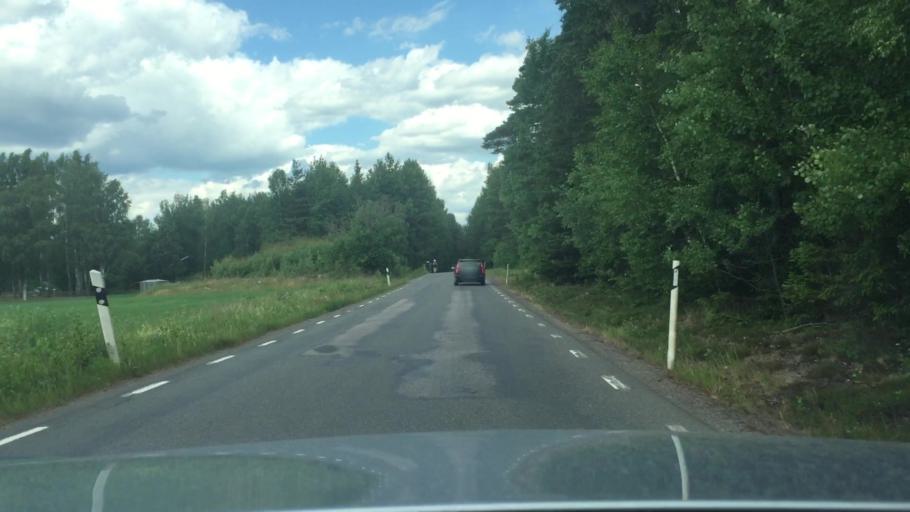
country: SE
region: Vaestra Goetaland
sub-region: Tidaholms Kommun
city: Tidaholm
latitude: 58.1996
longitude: 13.9793
